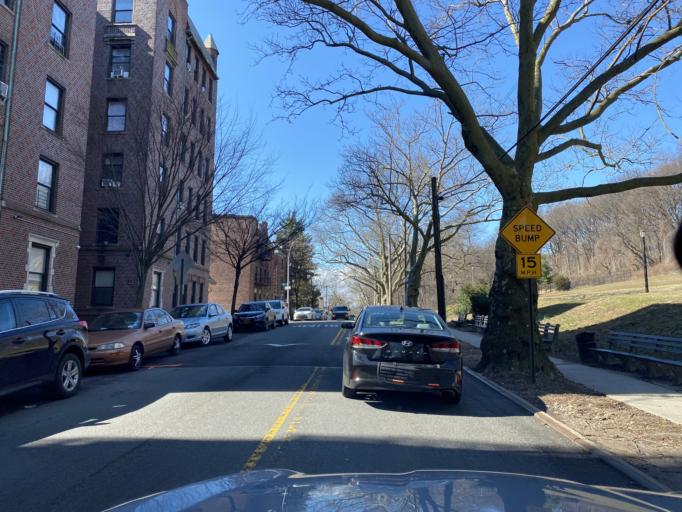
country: US
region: New York
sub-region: Queens County
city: Borough of Queens
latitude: 40.6967
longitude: -73.8587
